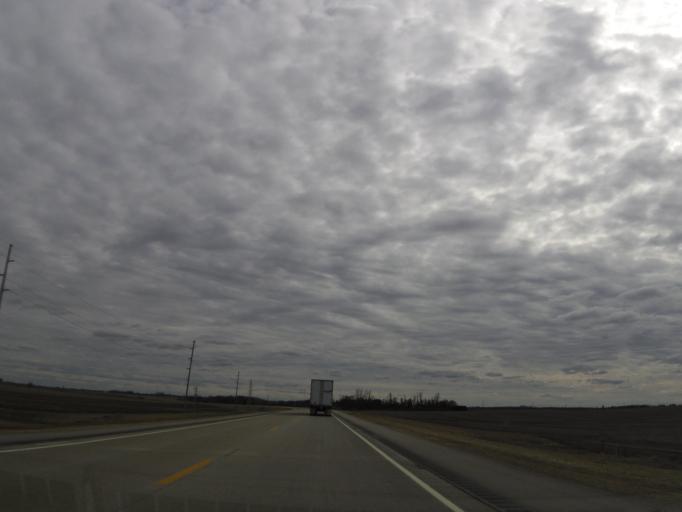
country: US
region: Minnesota
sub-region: Fillmore County
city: Spring Valley
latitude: 43.5662
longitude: -92.3891
